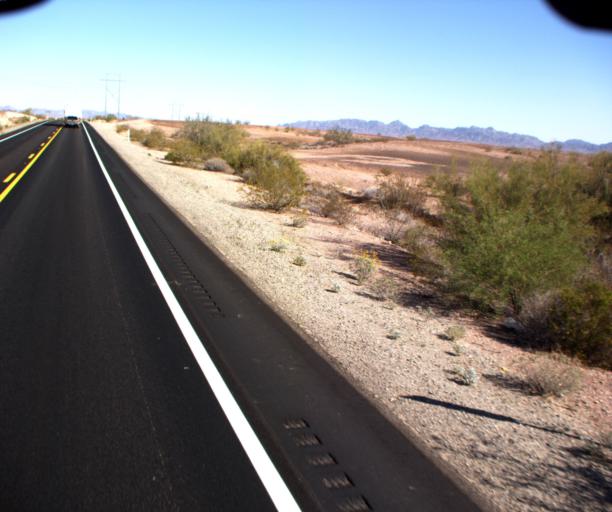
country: US
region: Arizona
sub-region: Yuma County
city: Wellton
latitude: 33.0178
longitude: -114.2864
